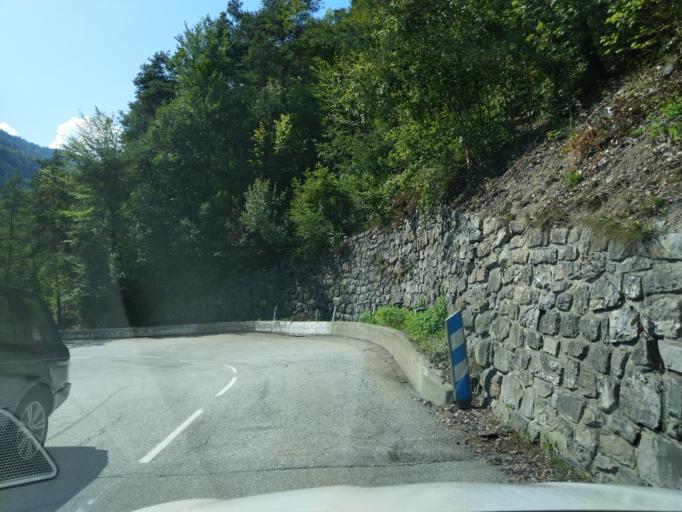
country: FR
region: Rhone-Alpes
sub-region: Departement de la Savoie
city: Les Allues
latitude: 45.4466
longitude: 6.5626
